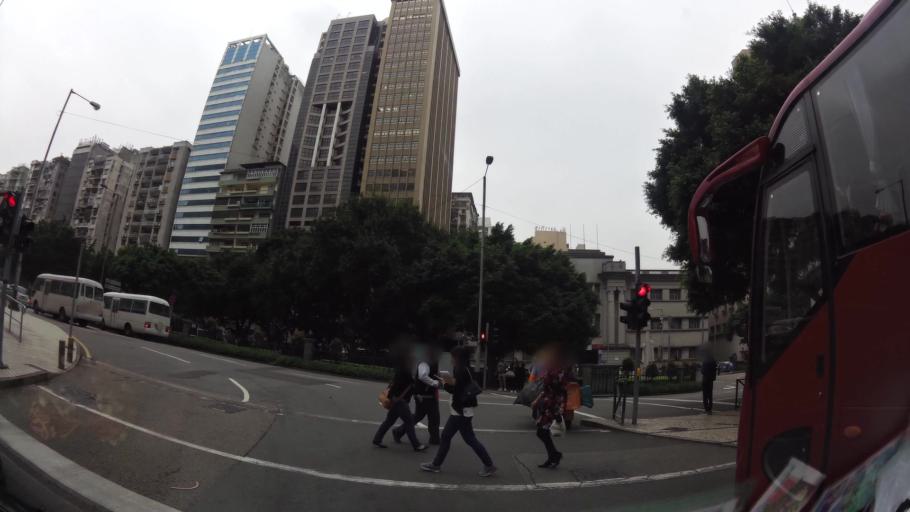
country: MO
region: Macau
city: Macau
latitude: 22.1913
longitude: 113.5406
